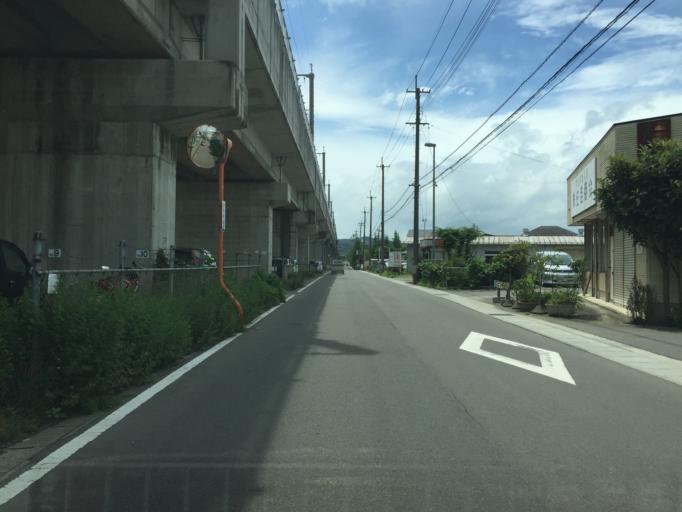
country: JP
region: Fukushima
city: Fukushima-shi
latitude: 37.7247
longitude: 140.4557
